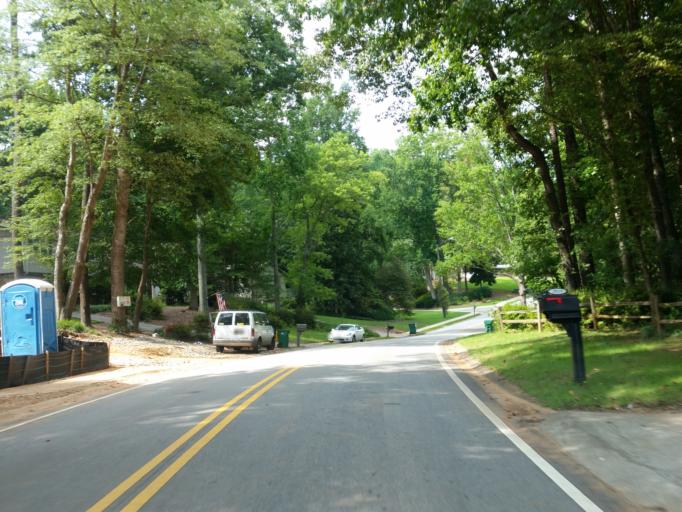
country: US
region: Georgia
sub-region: Fulton County
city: Sandy Springs
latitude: 33.9705
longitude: -84.4462
